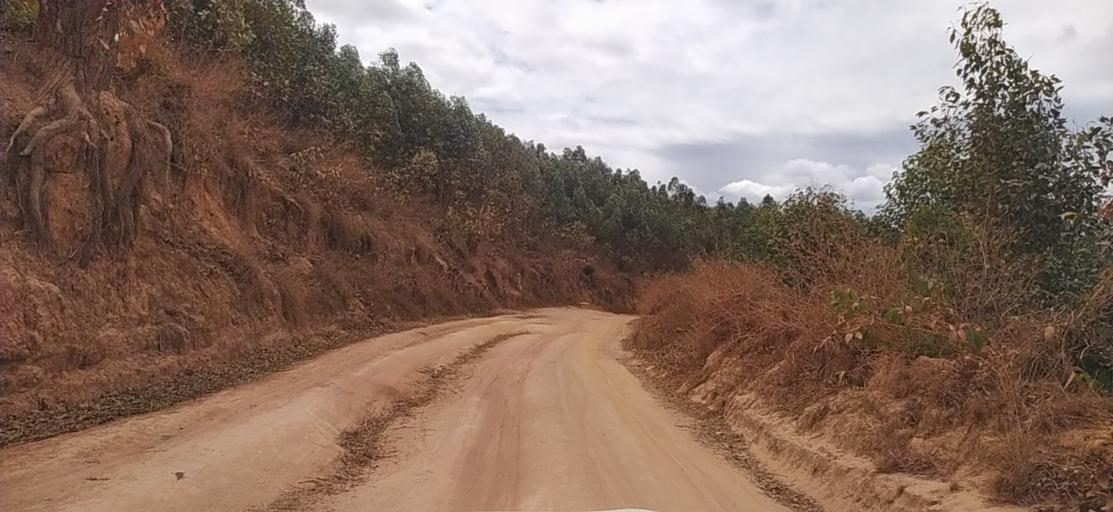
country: MG
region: Alaotra Mangoro
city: Ambatondrazaka
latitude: -18.0073
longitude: 48.2591
